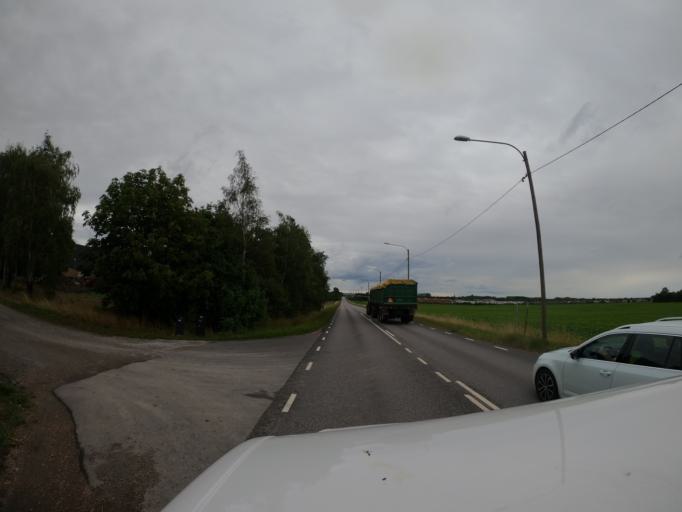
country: SE
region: Skane
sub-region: Lunds Kommun
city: Lund
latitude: 55.7360
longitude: 13.1987
